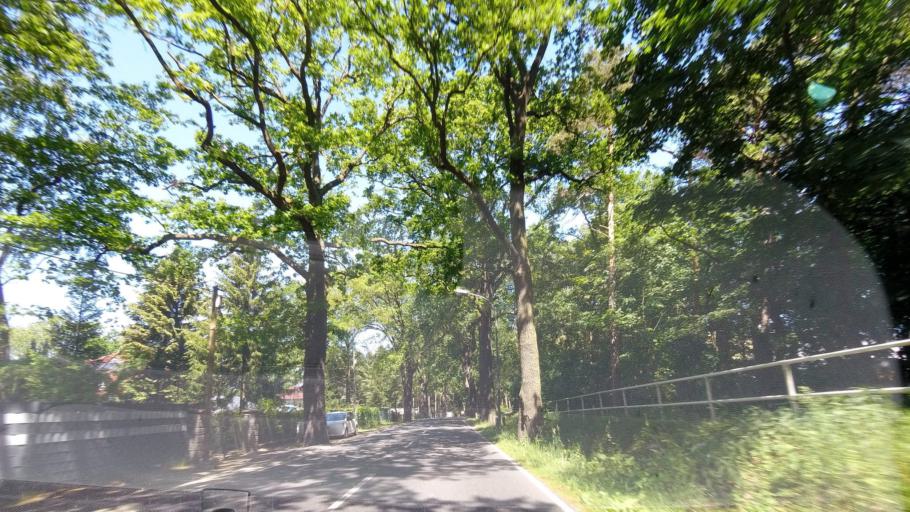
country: DE
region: Brandenburg
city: Ludwigsfelde
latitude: 52.2906
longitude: 13.2091
